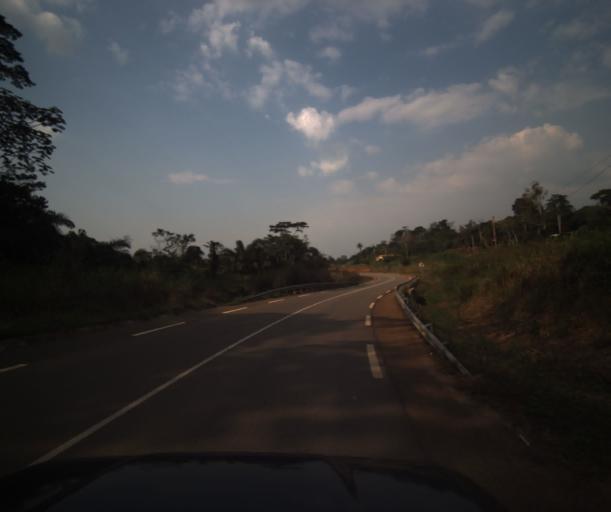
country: CM
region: Centre
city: Akono
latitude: 3.6427
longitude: 11.3286
